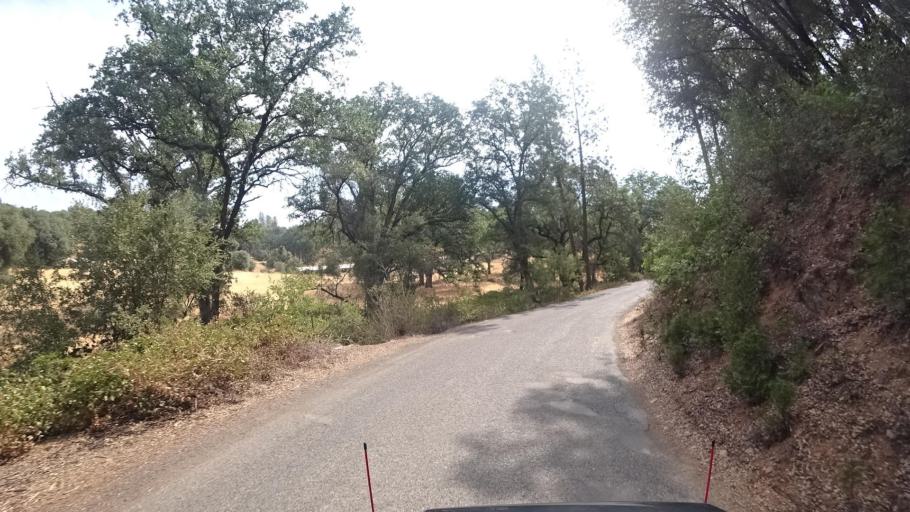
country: US
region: California
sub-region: Mariposa County
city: Midpines
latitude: 37.5629
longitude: -119.9718
